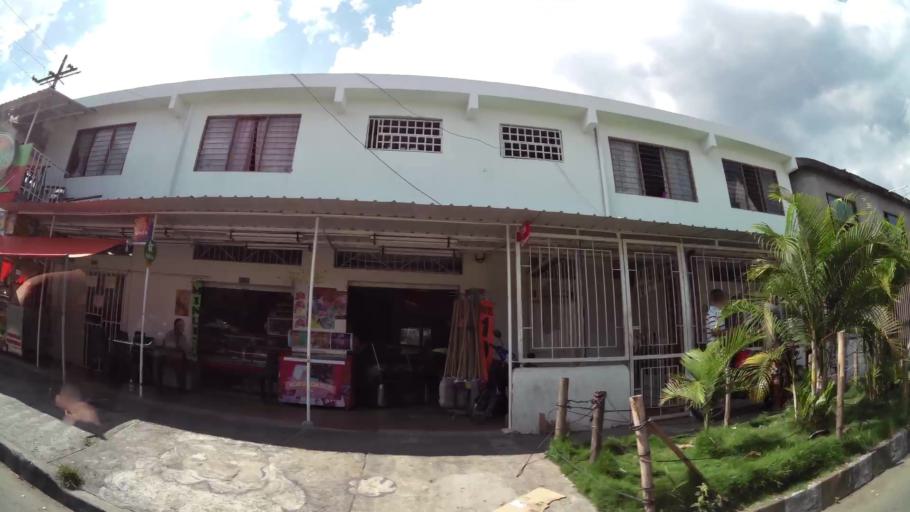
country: CO
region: Valle del Cauca
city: Cali
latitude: 3.3994
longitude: -76.5159
